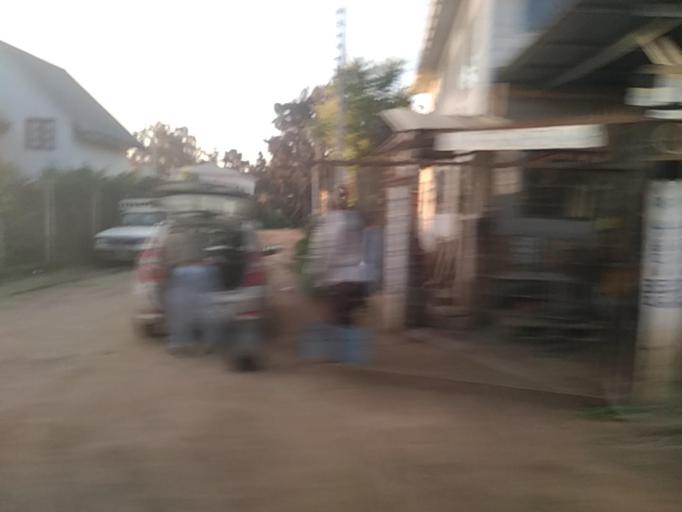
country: CL
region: Valparaiso
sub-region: San Antonio Province
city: El Tabo
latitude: -33.4541
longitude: -71.6573
